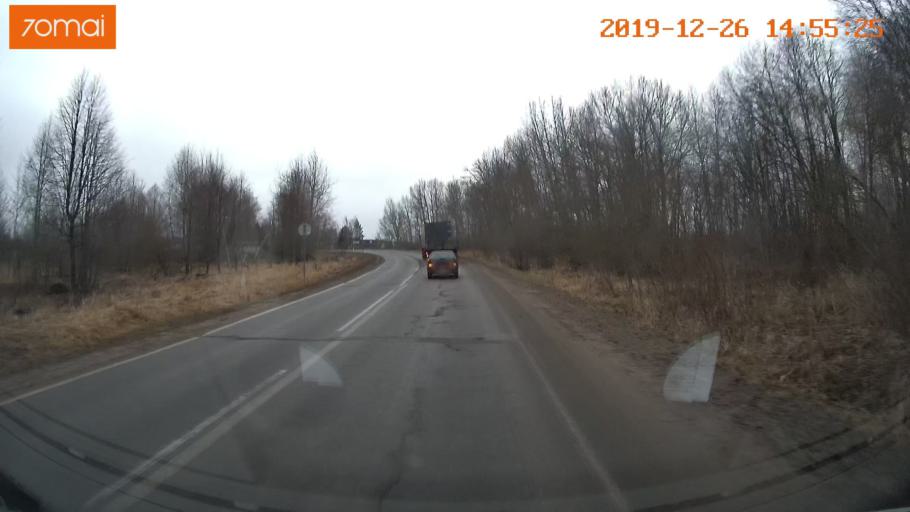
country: RU
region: Jaroslavl
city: Rybinsk
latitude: 58.3011
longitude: 38.8757
